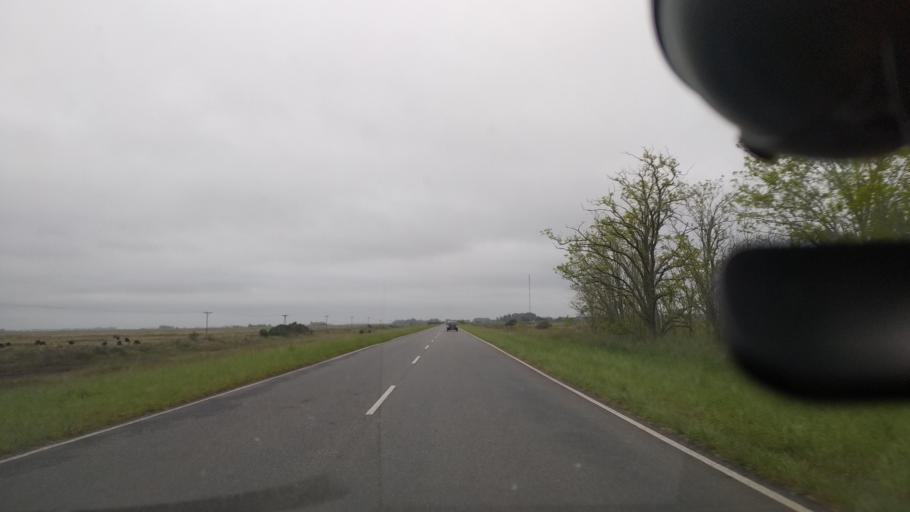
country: AR
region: Buenos Aires
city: Veronica
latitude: -35.4507
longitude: -57.3357
